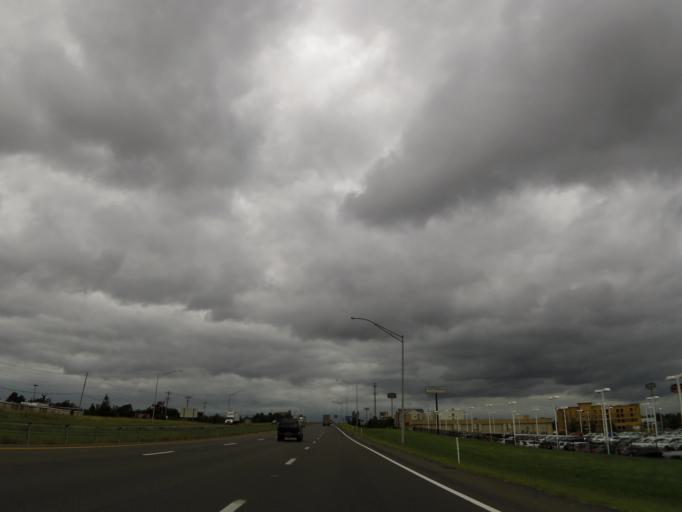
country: US
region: Kentucky
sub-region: McCracken County
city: Hendron
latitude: 37.0812
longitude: -88.6822
